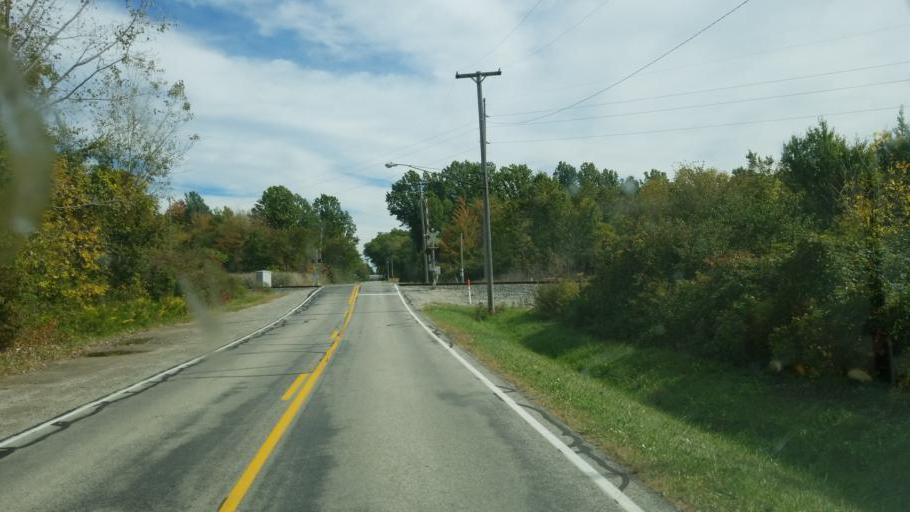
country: US
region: Ohio
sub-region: Erie County
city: Huron
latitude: 41.3647
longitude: -82.4621
